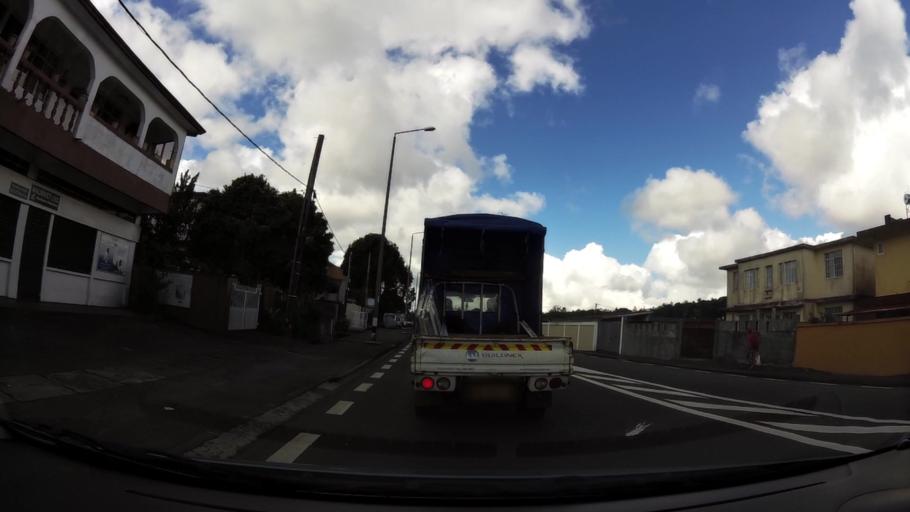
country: MU
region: Plaines Wilhems
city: Curepipe
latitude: -20.3236
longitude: 57.5339
